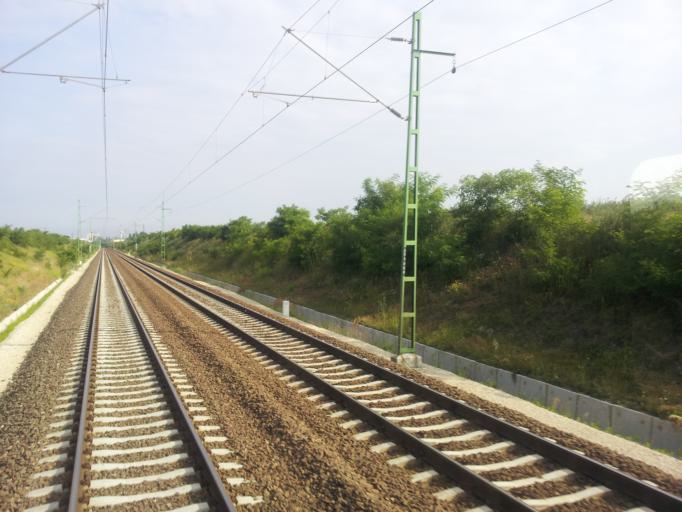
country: HU
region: Fejer
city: Szekesfehervar
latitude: 47.1770
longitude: 18.4557
